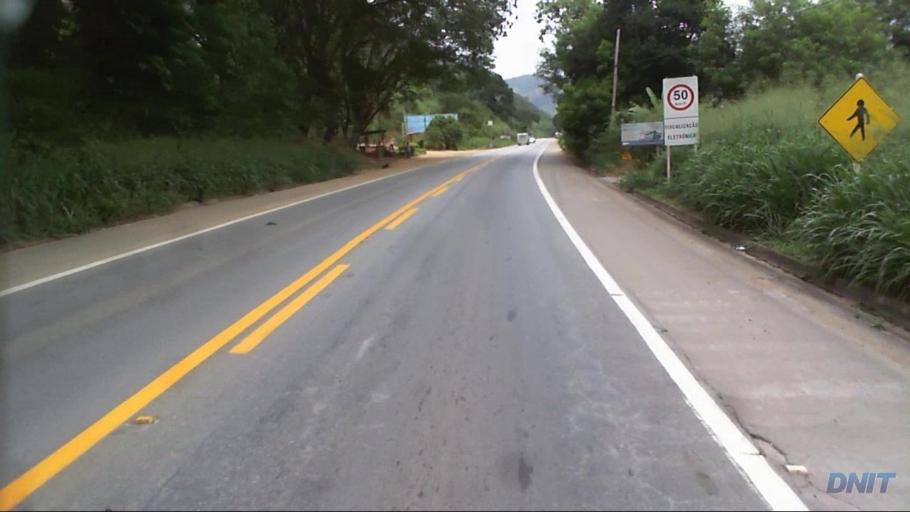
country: BR
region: Minas Gerais
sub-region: Timoteo
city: Timoteo
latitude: -19.5594
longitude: -42.7102
